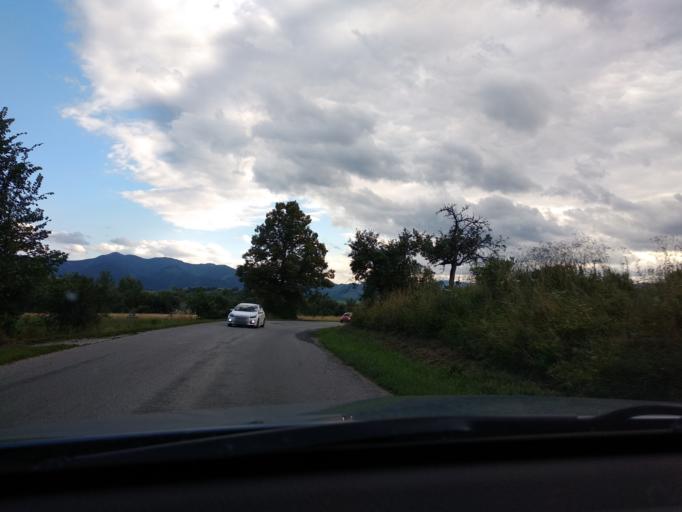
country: SK
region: Zilinsky
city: Ruzomberok
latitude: 49.0970
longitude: 19.3862
